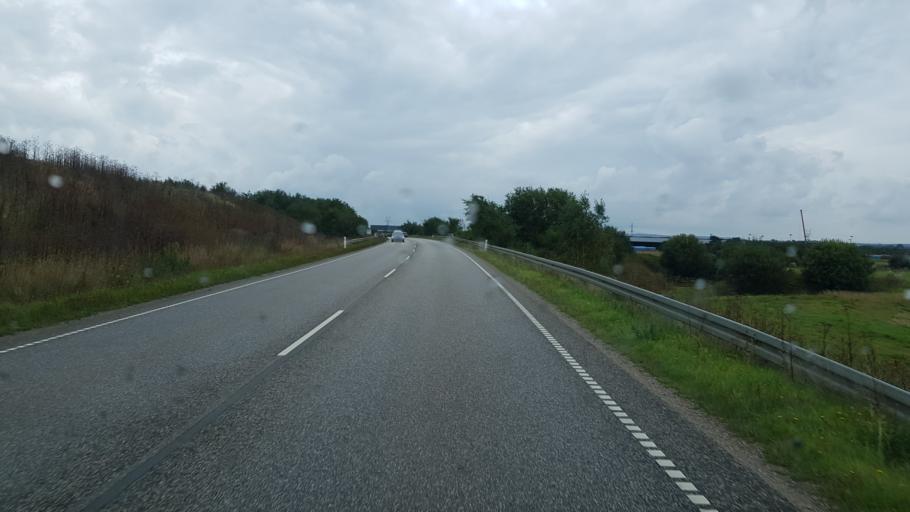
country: DK
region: Central Jutland
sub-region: Horsens Kommune
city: Horsens
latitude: 55.8921
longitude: 9.7613
